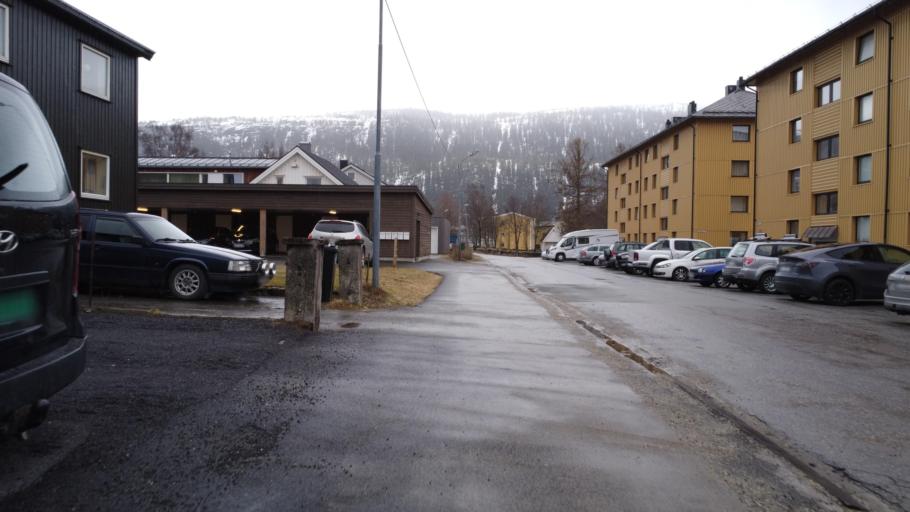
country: NO
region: Nordland
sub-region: Rana
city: Mo i Rana
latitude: 66.3113
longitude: 14.1460
